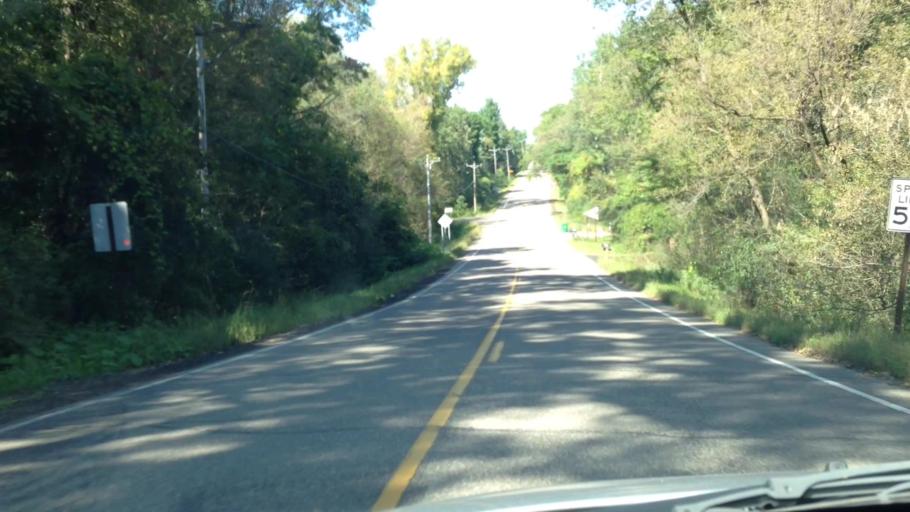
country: US
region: Minnesota
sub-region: Washington County
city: Stillwater
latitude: 45.0832
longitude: -92.8129
